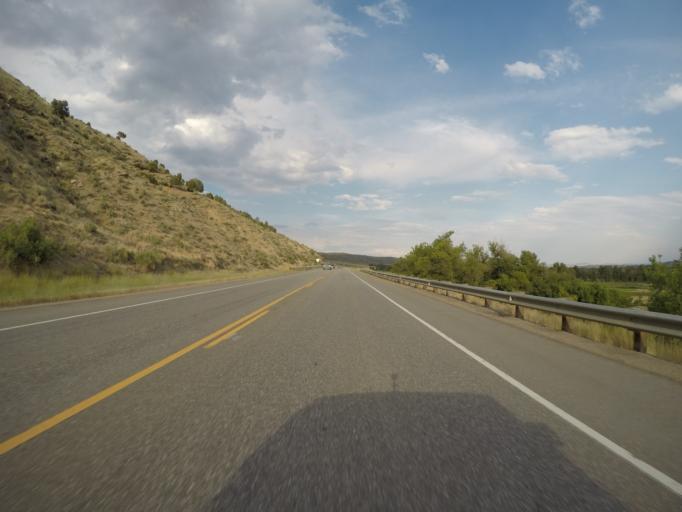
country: US
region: Colorado
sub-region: Moffat County
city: Craig
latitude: 40.5256
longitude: -107.4206
